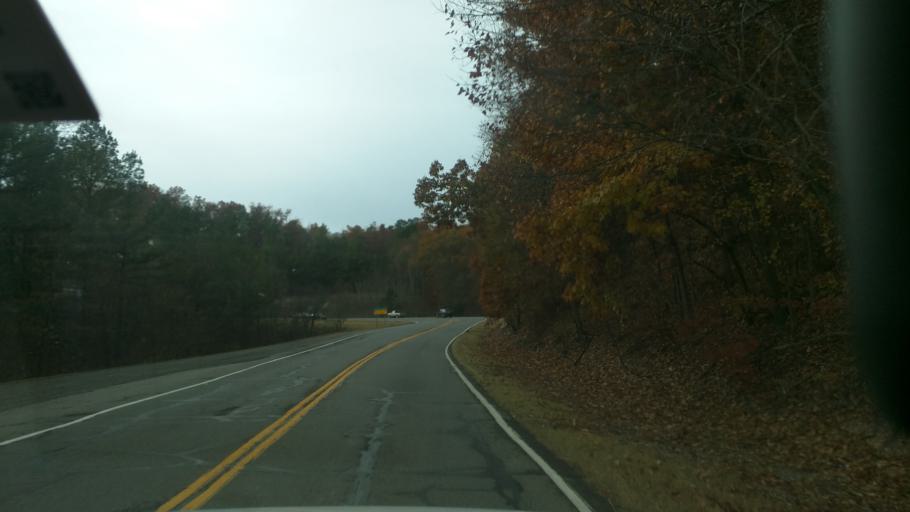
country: US
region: Oklahoma
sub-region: Cherokee County
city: Tahlequah
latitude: 35.9287
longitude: -94.8427
